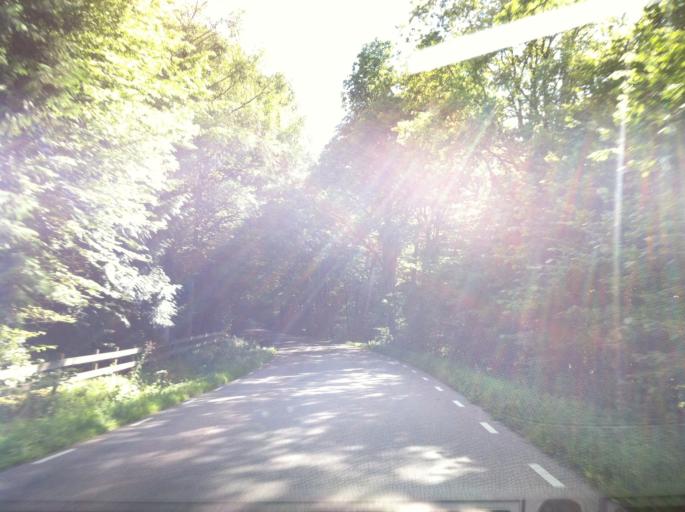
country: SE
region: Skane
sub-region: Hassleholms Kommun
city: Sosdala
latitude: 56.0247
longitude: 13.5766
